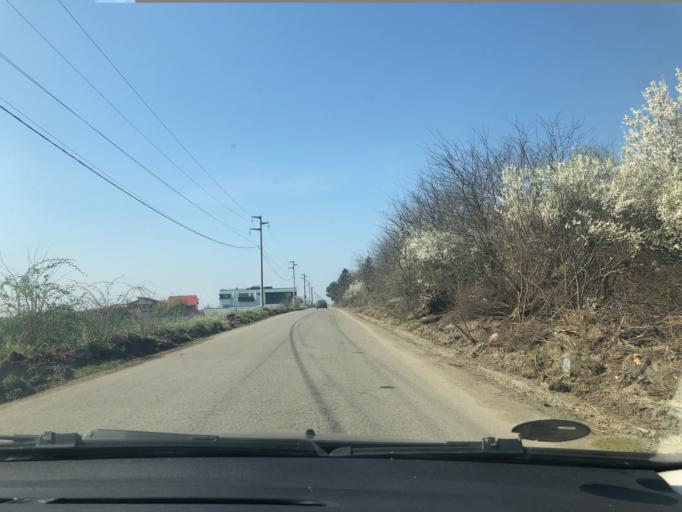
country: RO
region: Ilfov
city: Domnesti-Sarbi
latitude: 44.3675
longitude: 25.9164
